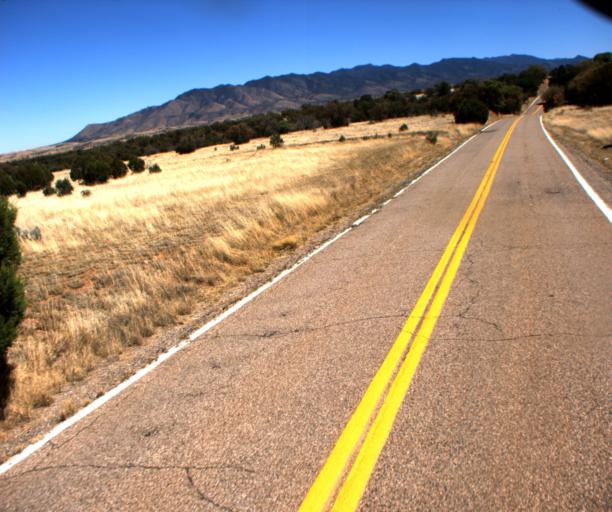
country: US
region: Arizona
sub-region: Cochise County
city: Huachuca City
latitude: 31.5534
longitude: -110.5495
